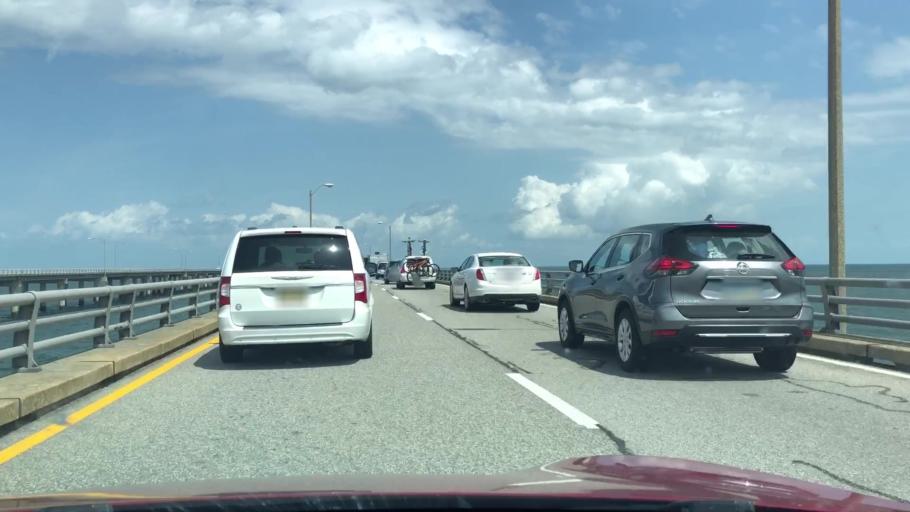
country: US
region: Virginia
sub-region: City of Virginia Beach
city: Virginia Beach
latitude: 36.9362
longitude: -76.1235
